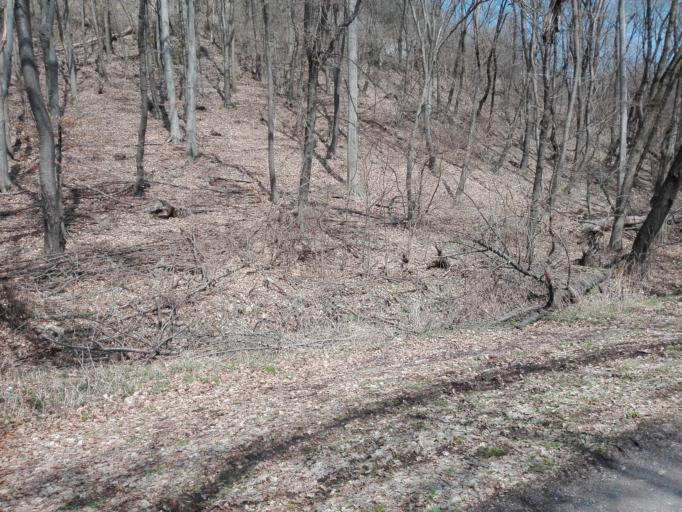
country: HU
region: Borsod-Abauj-Zemplen
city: Gonc
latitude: 48.5528
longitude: 21.4562
